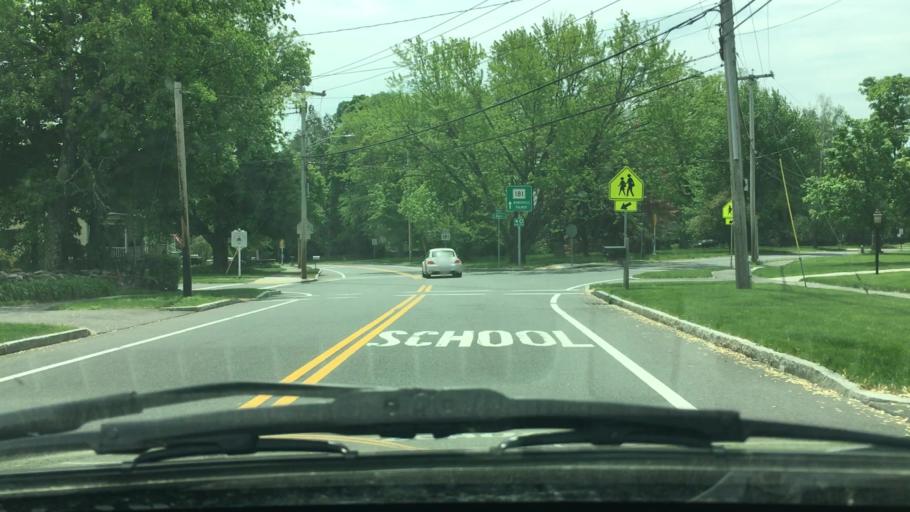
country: US
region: Massachusetts
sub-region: Hampshire County
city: Belchertown
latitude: 42.2738
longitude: -72.3985
